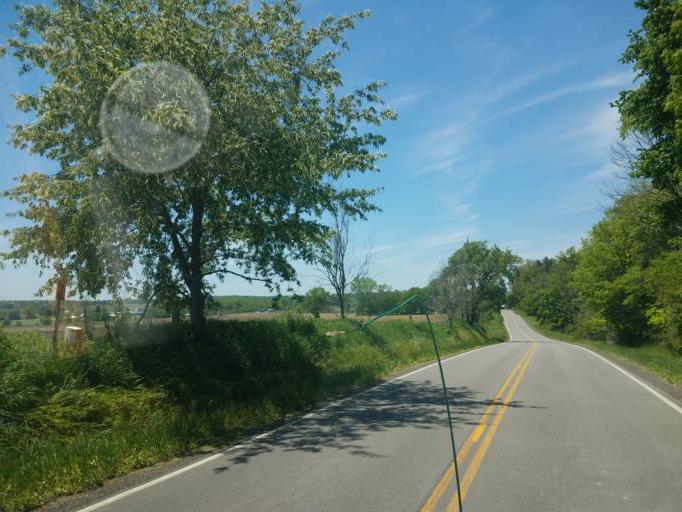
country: US
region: Ohio
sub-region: Ashland County
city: Ashland
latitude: 40.9603
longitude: -82.3542
